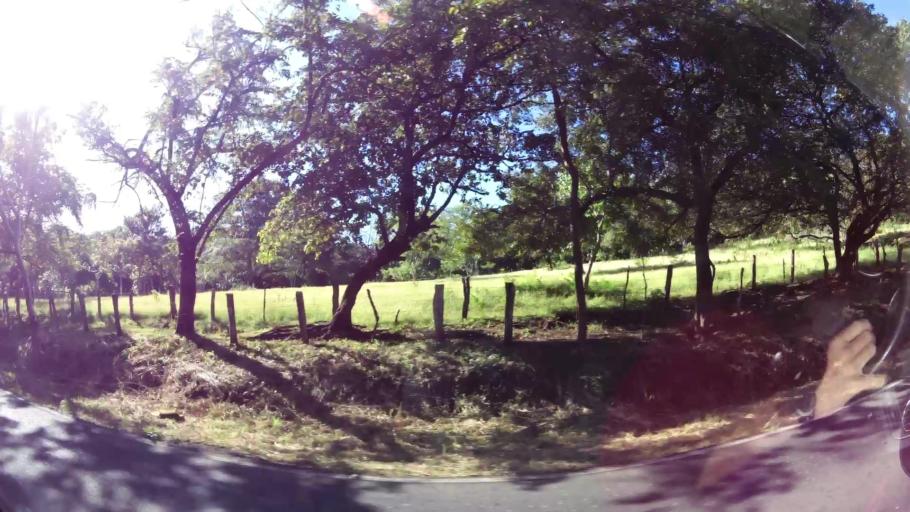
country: CR
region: Guanacaste
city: Belen
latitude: 10.3631
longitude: -85.6513
